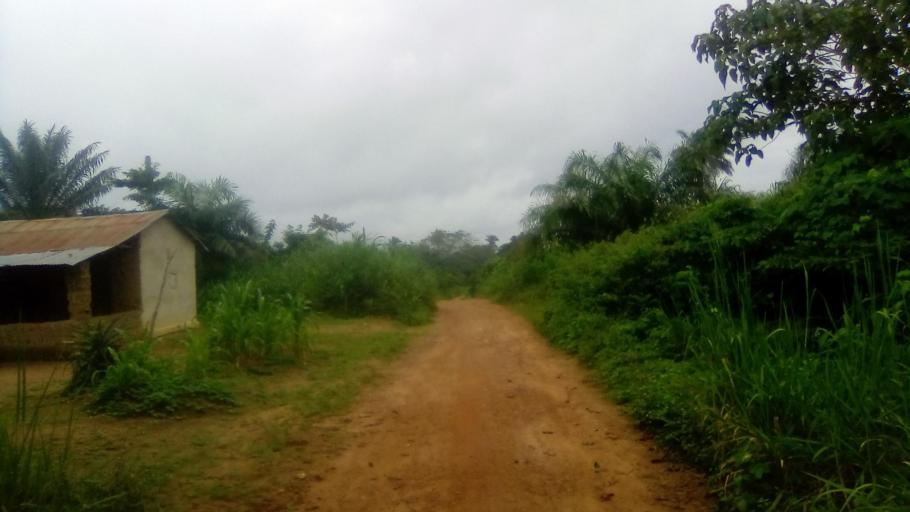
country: SL
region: Eastern Province
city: Kailahun
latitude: 8.2954
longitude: -10.5552
